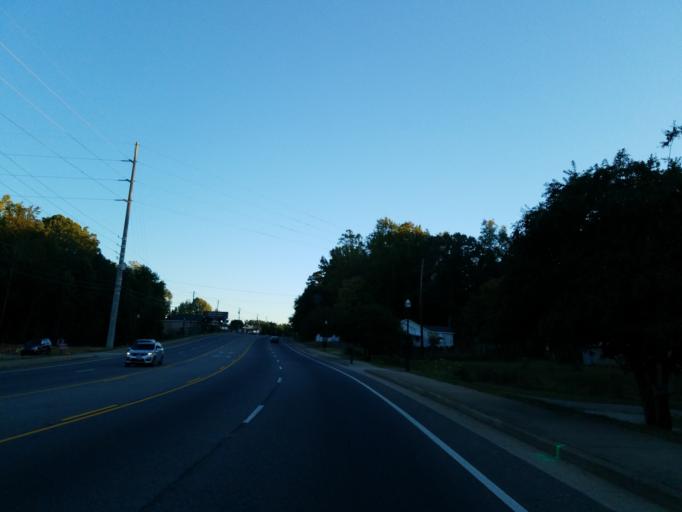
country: US
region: Georgia
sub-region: Forsyth County
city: Cumming
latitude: 34.1966
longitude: -84.1411
